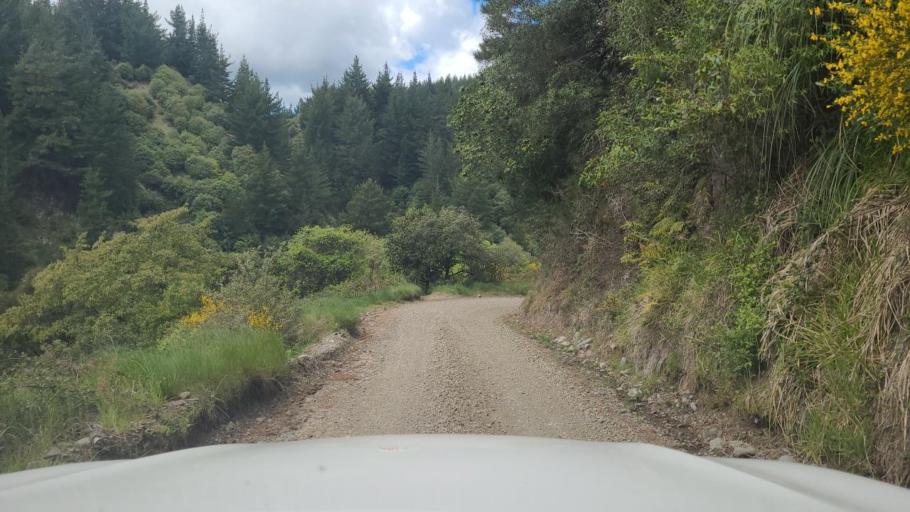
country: NZ
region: Hawke's Bay
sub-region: Napier City
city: Taradale
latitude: -39.1842
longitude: 176.6339
